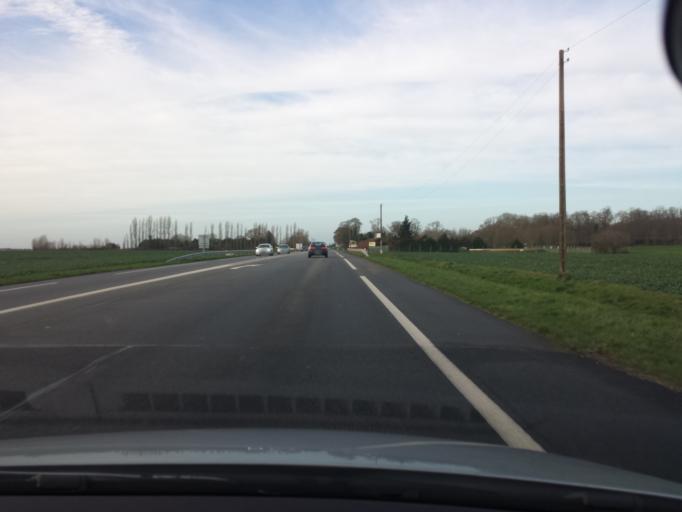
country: FR
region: Haute-Normandie
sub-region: Departement de l'Eure
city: Gravigny
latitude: 49.0138
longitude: 1.2498
